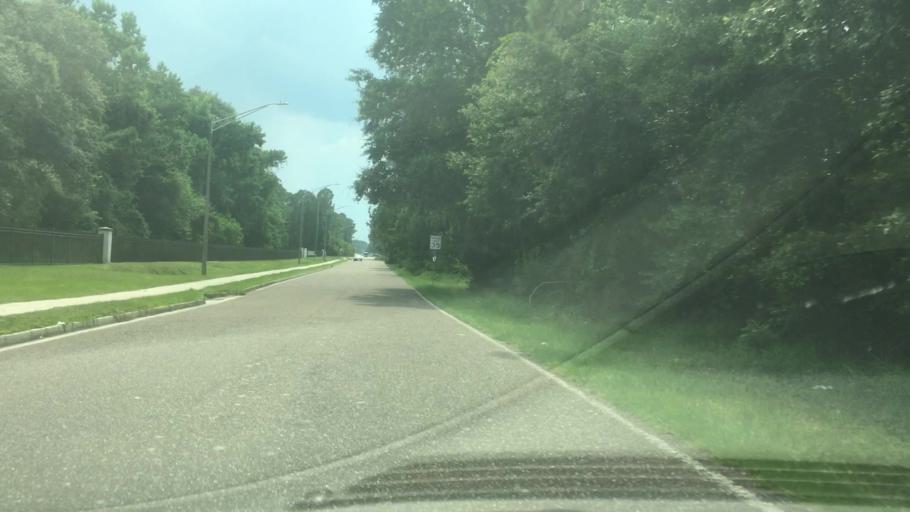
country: US
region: Florida
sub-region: Duval County
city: Neptune Beach
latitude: 30.3021
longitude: -81.5065
